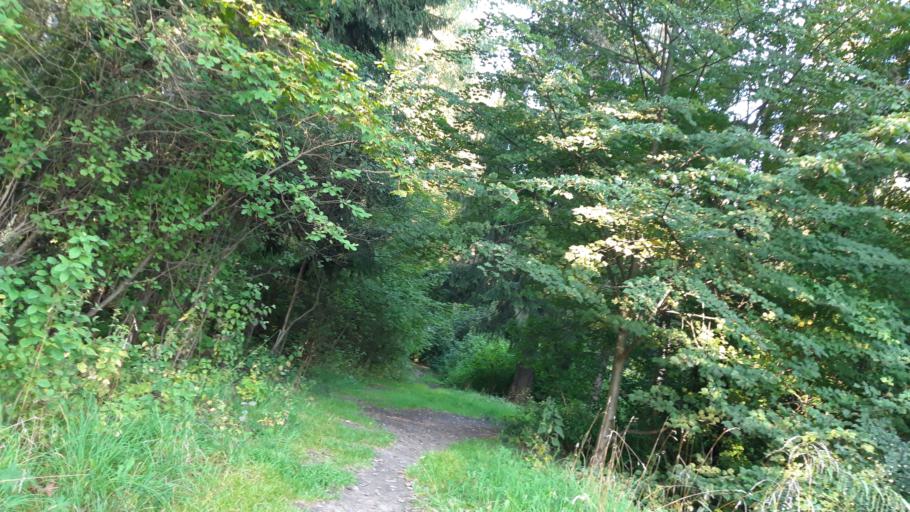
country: RU
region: Moscow
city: Zelenograd
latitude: 55.9883
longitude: 37.1913
